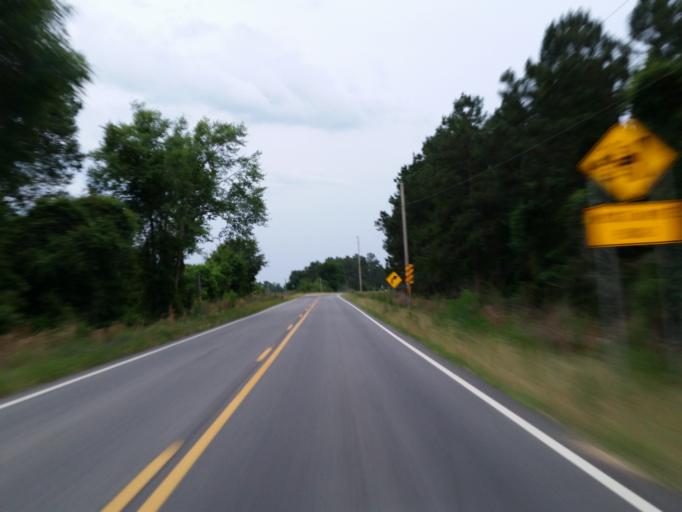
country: US
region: Georgia
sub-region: Crisp County
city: Cordele
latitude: 31.8562
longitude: -83.7450
